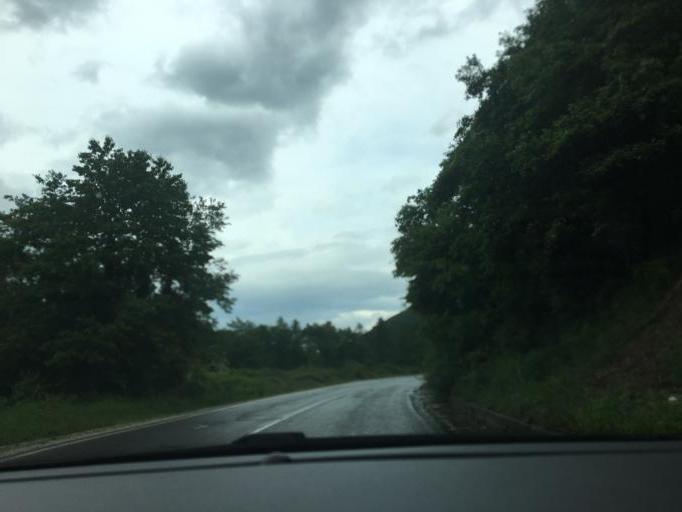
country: MK
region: Debarca
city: Meseista
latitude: 41.2697
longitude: 20.7788
